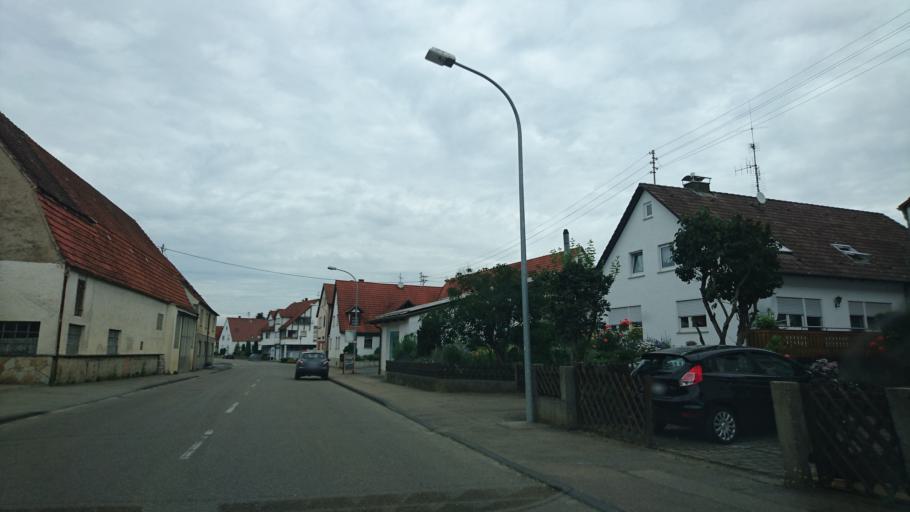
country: DE
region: Baden-Wuerttemberg
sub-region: Regierungsbezirk Stuttgart
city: Sontheim an der Brenz
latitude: 48.5498
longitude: 10.2938
